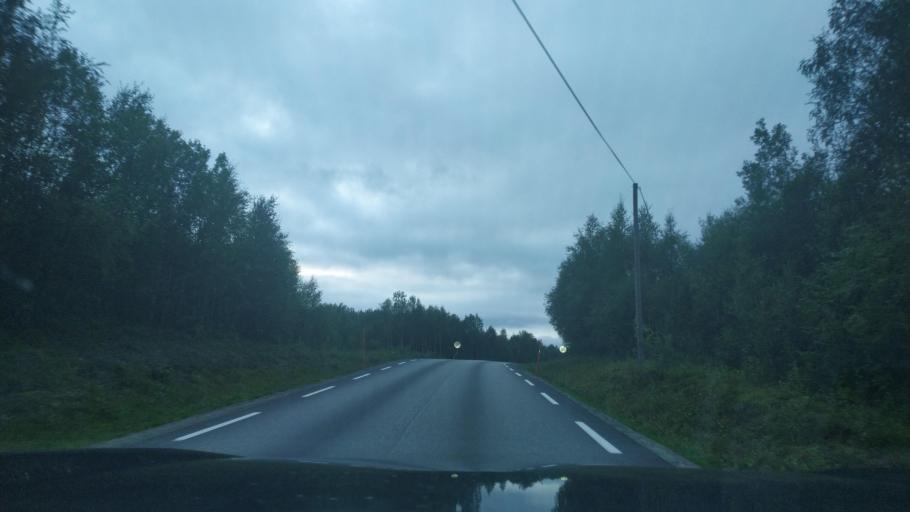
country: NO
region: Troms
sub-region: Lavangen
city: Tennevoll
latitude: 68.7274
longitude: 17.8280
